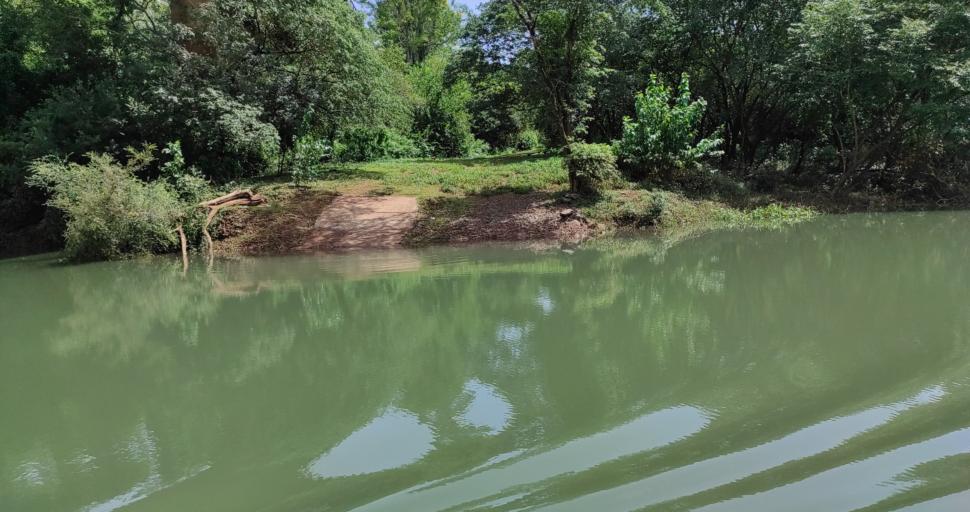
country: AR
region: Misiones
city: El Soberbio
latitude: -27.2803
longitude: -54.1966
